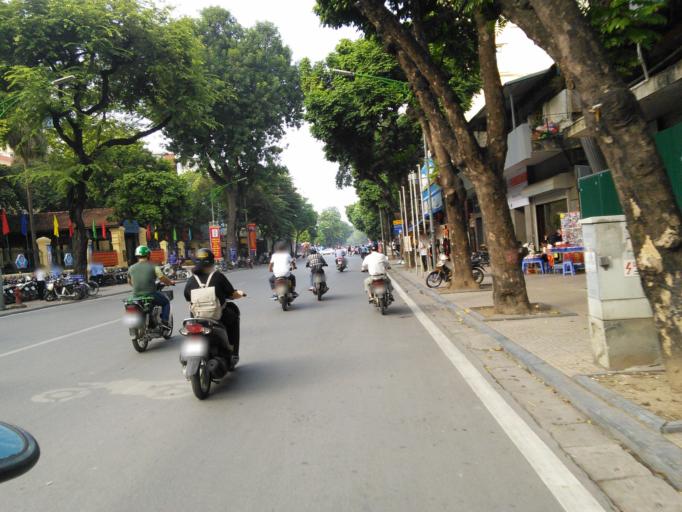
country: VN
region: Ha Noi
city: Hoan Kiem
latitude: 21.0229
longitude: 105.8527
